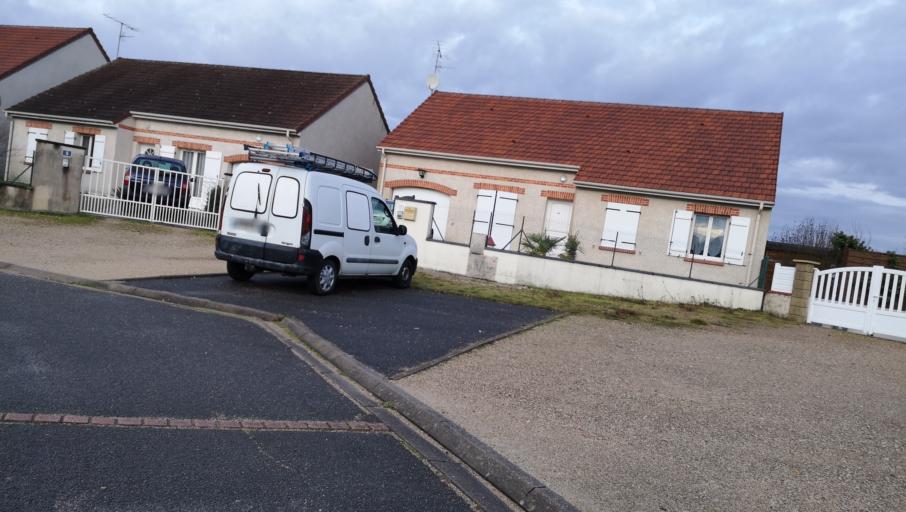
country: FR
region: Centre
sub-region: Departement du Loiret
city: Saint-Jean-de-Braye
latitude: 47.9233
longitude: 1.9668
